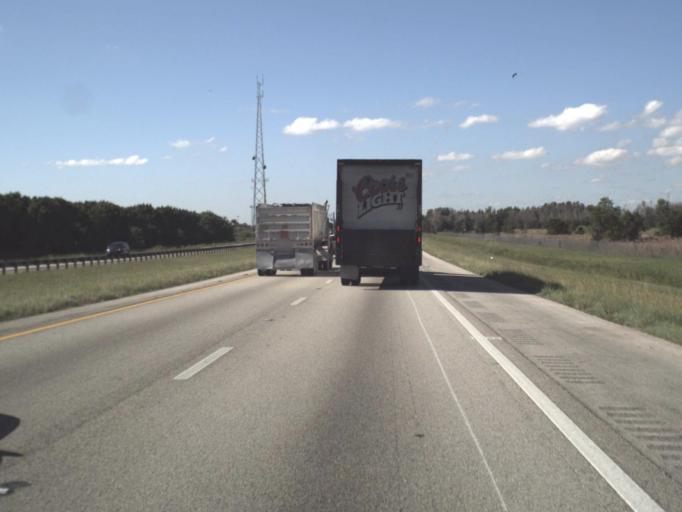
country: US
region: Florida
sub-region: Miami-Dade County
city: Country Club
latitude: 25.9626
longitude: -80.3347
